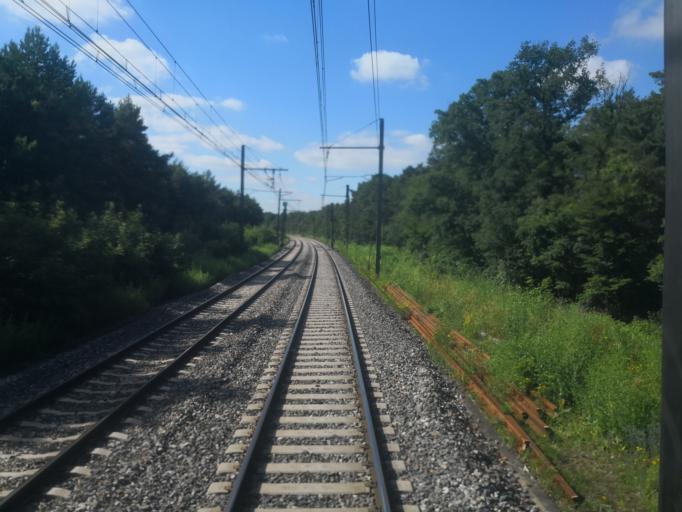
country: FR
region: Ile-de-France
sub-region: Departement de Seine-et-Marne
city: Samois-sur-Seine
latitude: 48.4393
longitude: 2.7371
